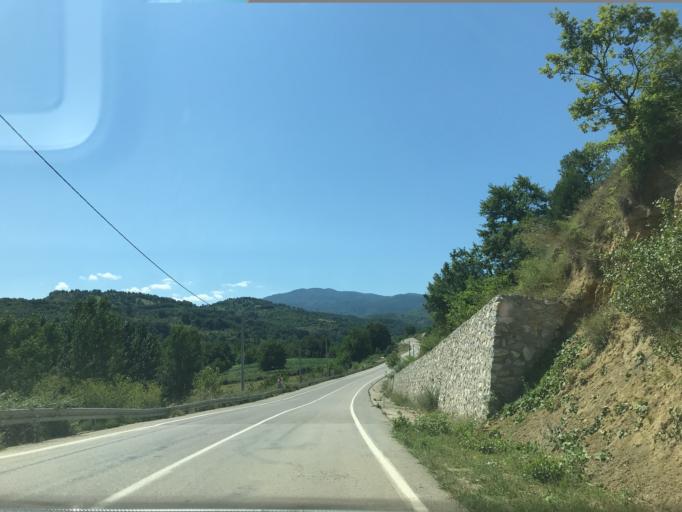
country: TR
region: Bursa
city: Tahtakopru
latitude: 39.9795
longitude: 29.6043
